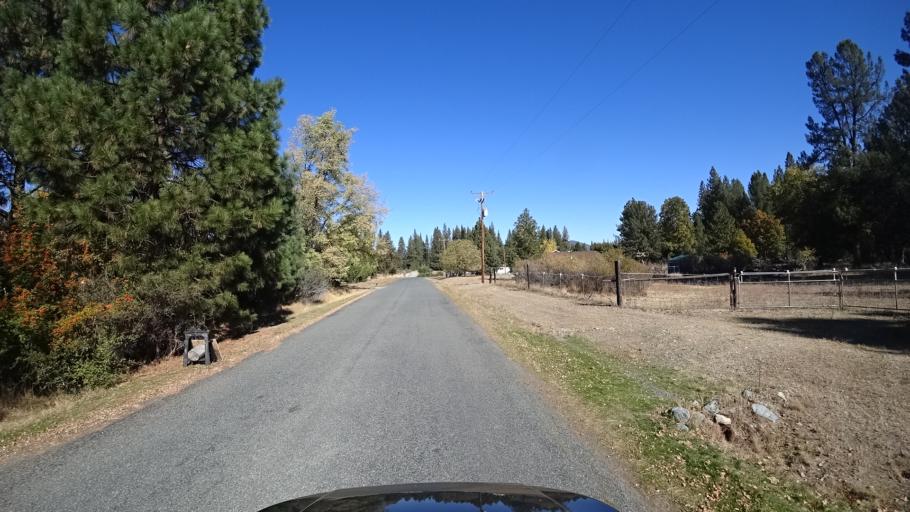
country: US
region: California
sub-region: Siskiyou County
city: Yreka
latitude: 41.5256
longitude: -122.9192
